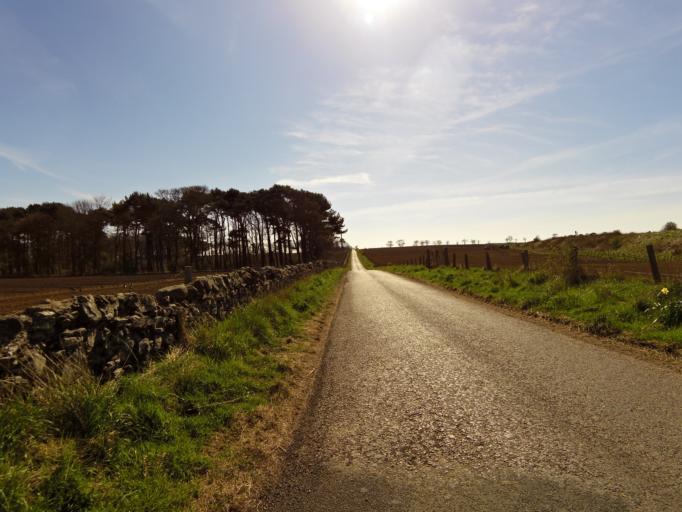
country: GB
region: Scotland
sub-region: Angus
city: Montrose
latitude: 56.6895
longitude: -2.4608
